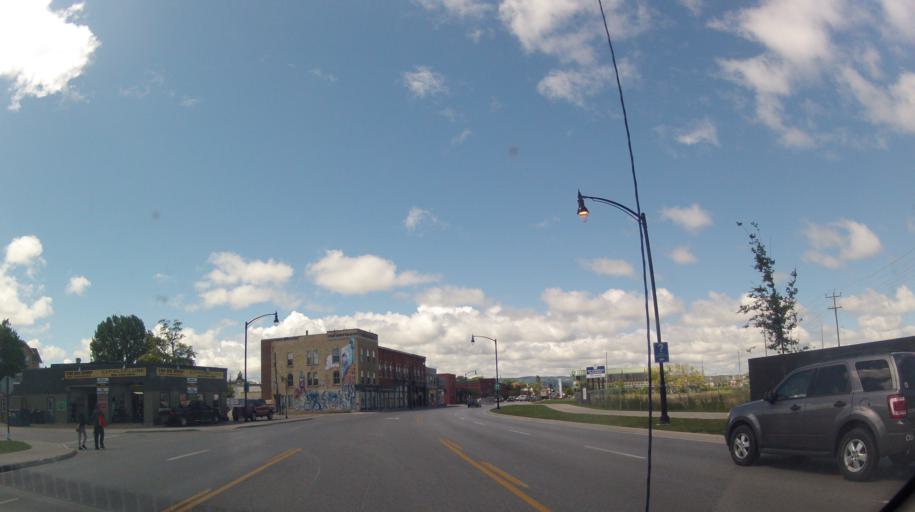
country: CA
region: Ontario
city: Collingwood
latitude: 44.5033
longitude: -80.2150
